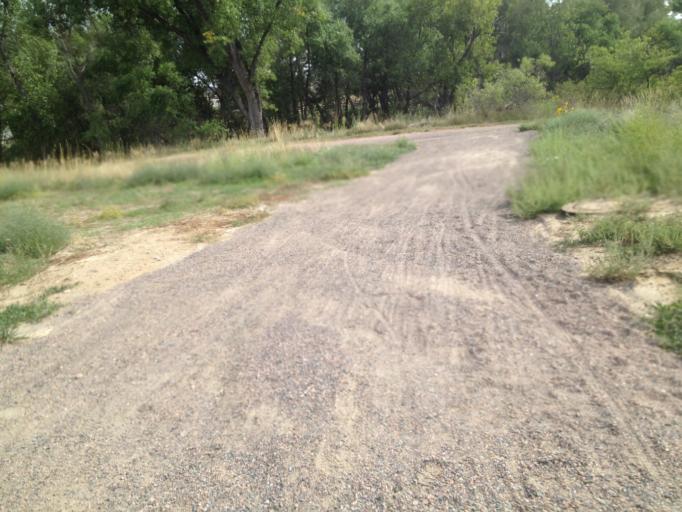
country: US
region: Colorado
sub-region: Boulder County
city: Lafayette
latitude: 39.9803
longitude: -105.1018
